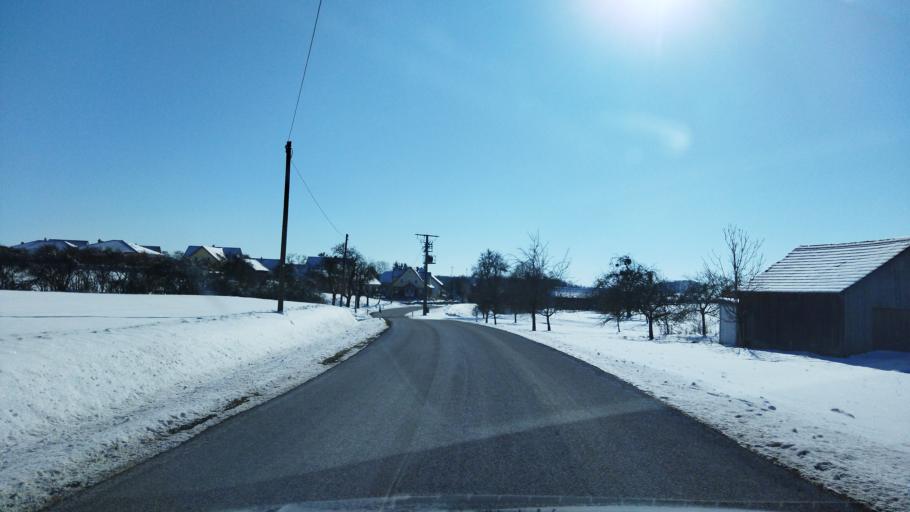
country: DE
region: Baden-Wuerttemberg
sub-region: Regierungsbezirk Stuttgart
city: Langenburg
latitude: 49.2526
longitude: 9.8920
